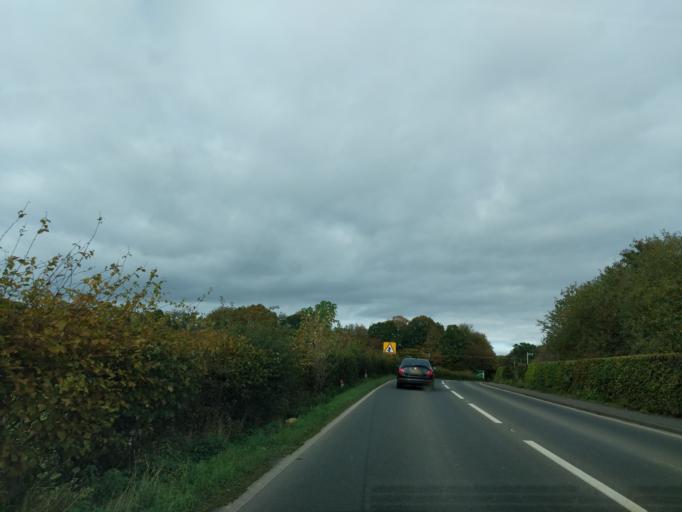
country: GB
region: Scotland
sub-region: Dumfries and Galloway
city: Thornhill
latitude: 55.2477
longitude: -3.7717
